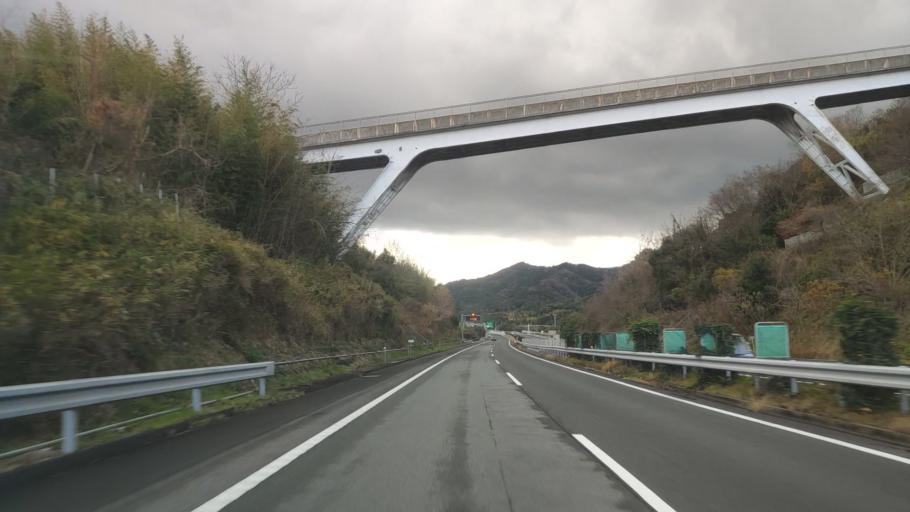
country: JP
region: Hyogo
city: Sumoto
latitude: 34.3460
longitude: 134.8489
